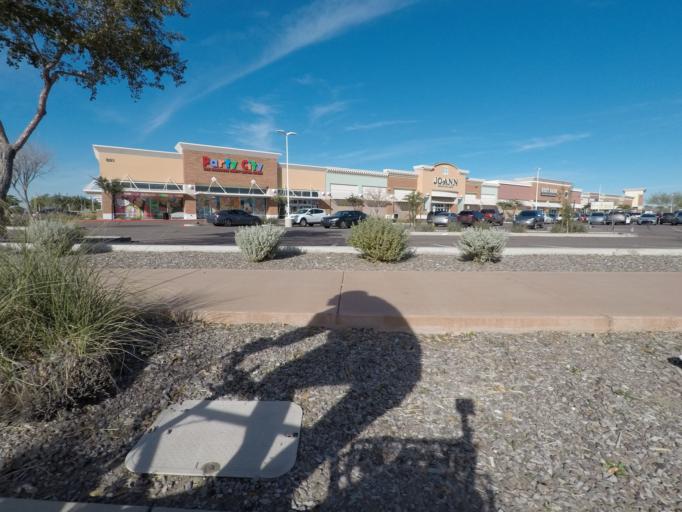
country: US
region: Arizona
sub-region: Maricopa County
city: Tempe
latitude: 33.4311
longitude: -111.8712
